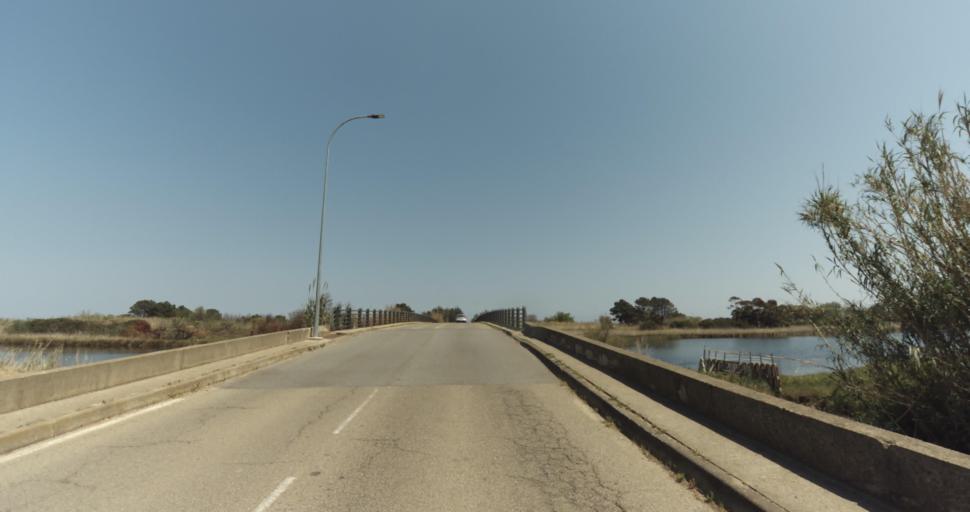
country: FR
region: Corsica
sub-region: Departement de la Haute-Corse
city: Biguglia
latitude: 42.6545
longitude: 9.4475
